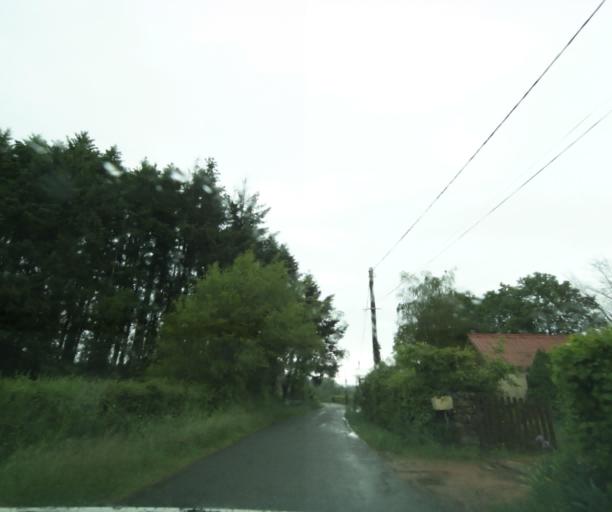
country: FR
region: Bourgogne
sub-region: Departement de Saone-et-Loire
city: Ciry-le-Noble
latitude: 46.5373
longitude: 4.3015
